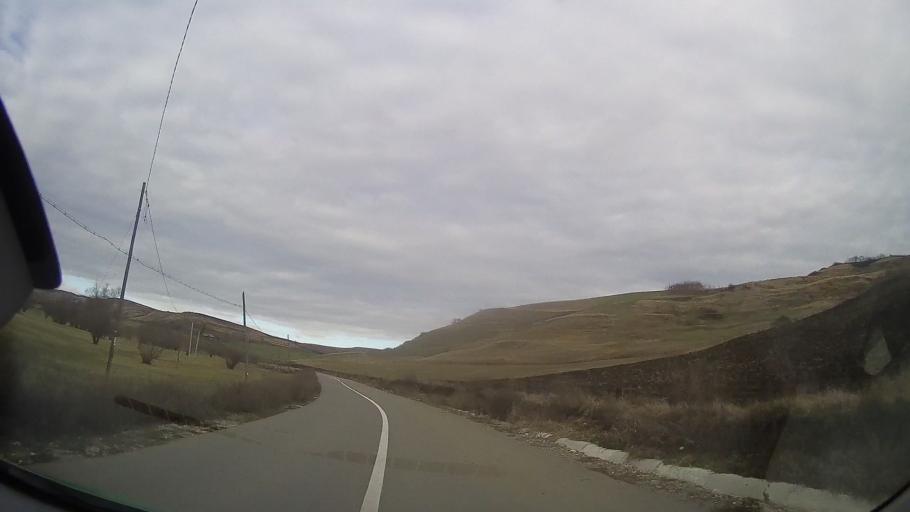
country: RO
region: Bistrita-Nasaud
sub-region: Comuna Silvasu de Campie
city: Silvasu de Campie
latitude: 46.8154
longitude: 24.2974
